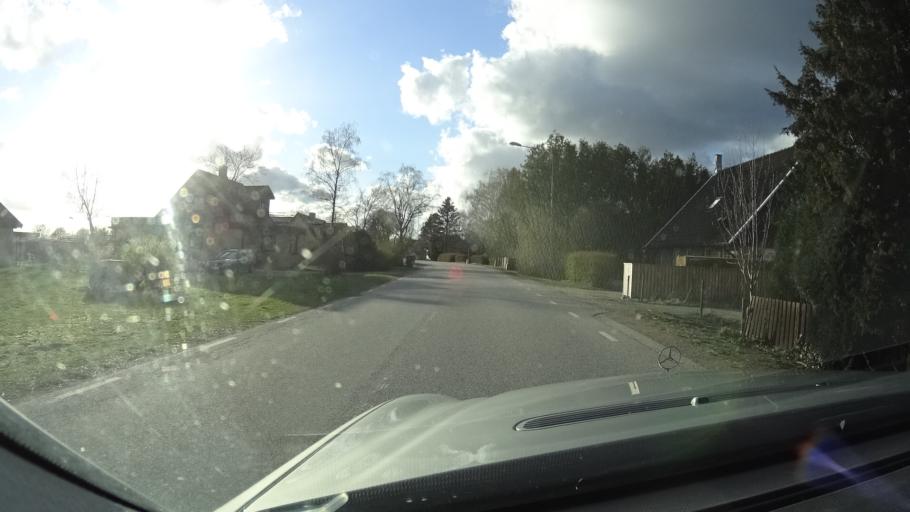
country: SE
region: Skane
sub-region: Hoors Kommun
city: Satofta
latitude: 55.9018
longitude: 13.6073
